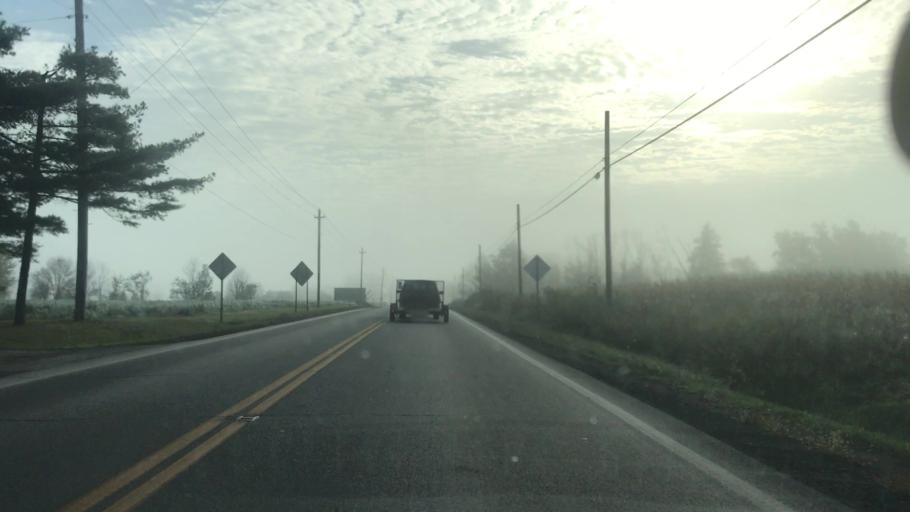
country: US
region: Ohio
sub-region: Geauga County
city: Middlefield
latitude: 41.4603
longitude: -81.0479
